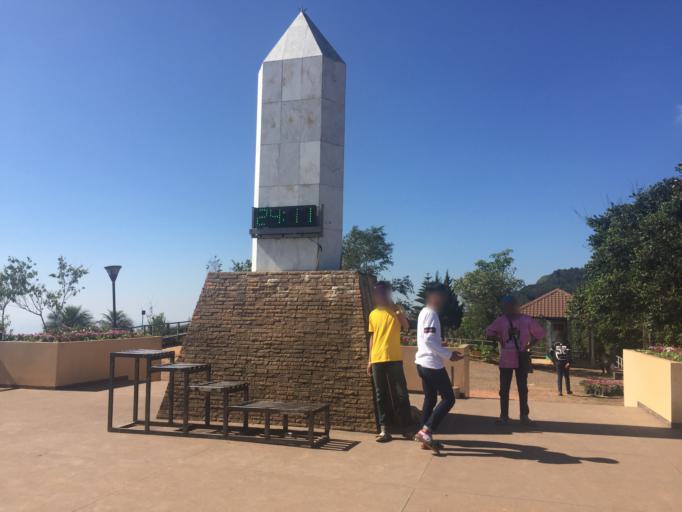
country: TH
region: Phetchabun
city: Lom Kao
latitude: 16.8967
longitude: 101.1061
